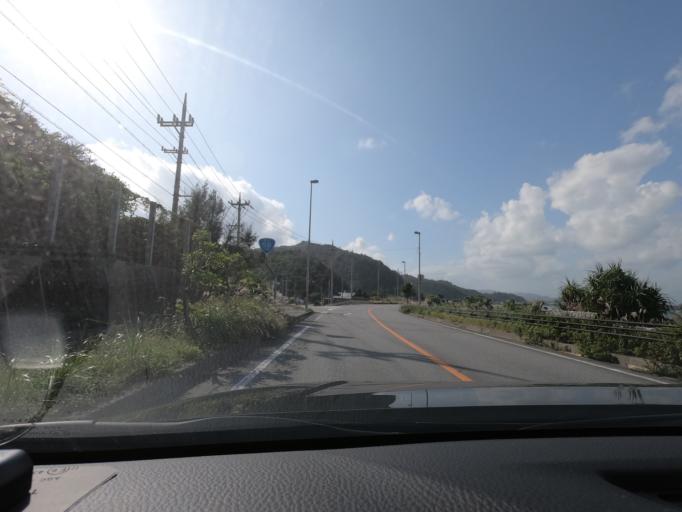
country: JP
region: Okinawa
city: Nago
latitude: 26.7577
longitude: 128.1892
